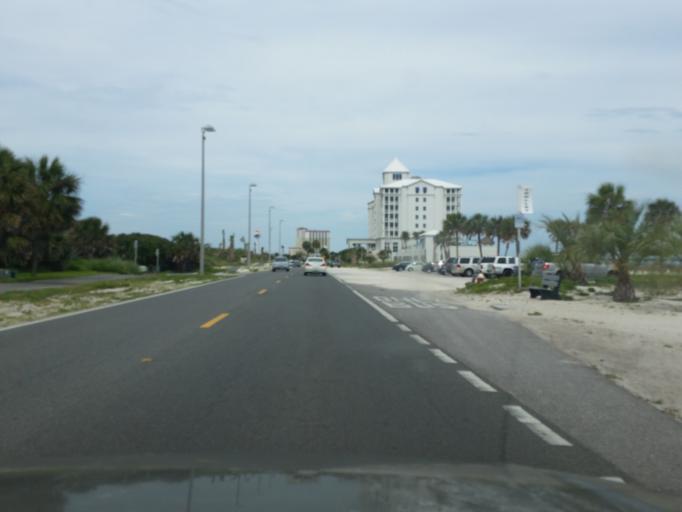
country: US
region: Florida
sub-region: Santa Rosa County
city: Gulf Breeze
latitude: 30.3299
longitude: -87.1504
